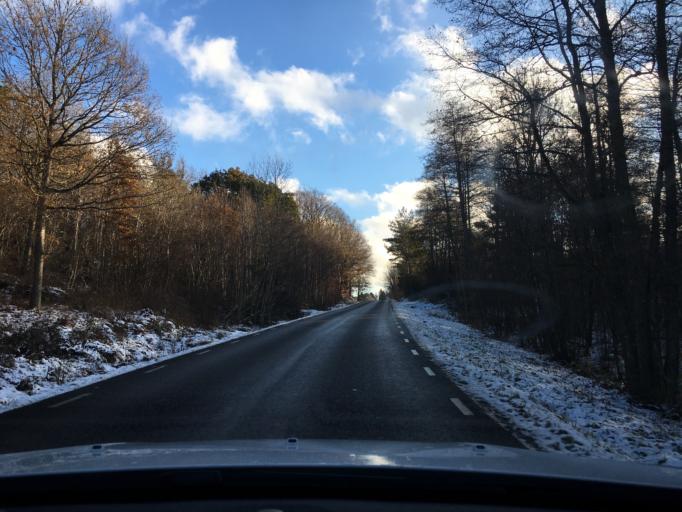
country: SE
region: Vaestra Goetaland
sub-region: Tjorns Kommun
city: Myggenas
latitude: 58.0582
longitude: 11.6923
